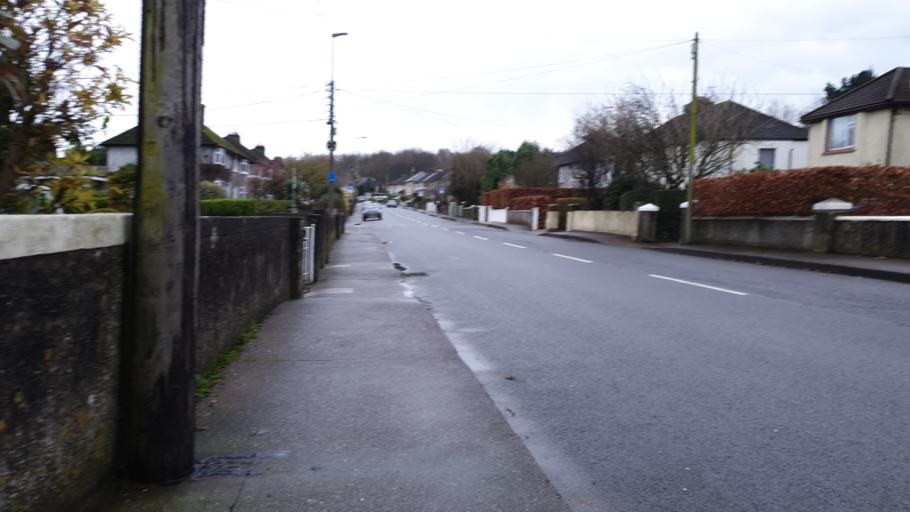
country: IE
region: Munster
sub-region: County Cork
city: Cork
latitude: 51.8949
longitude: -8.4308
